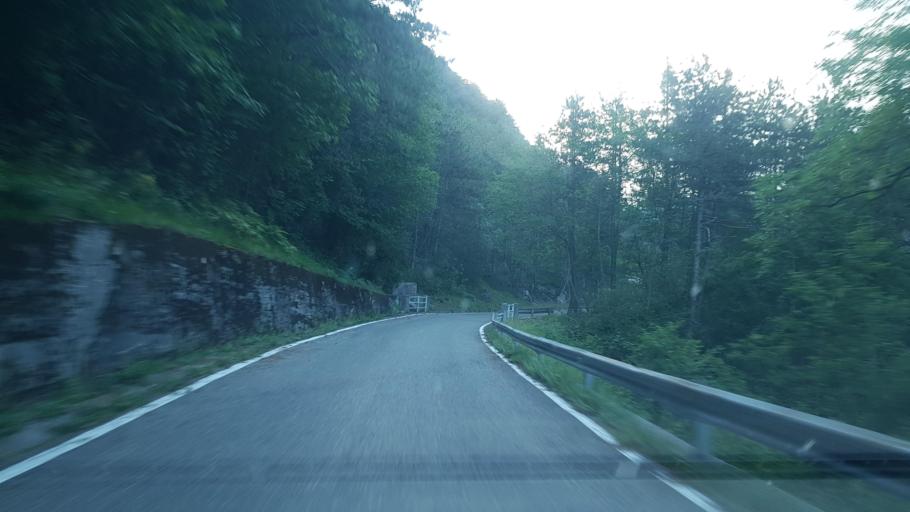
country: IT
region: Friuli Venezia Giulia
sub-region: Provincia di Udine
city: Dogna
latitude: 46.4487
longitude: 13.3473
